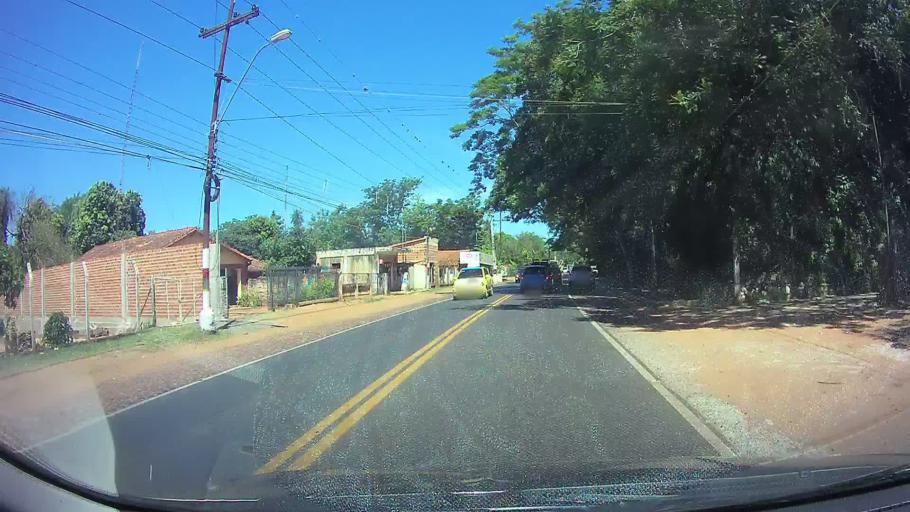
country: PY
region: Central
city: Aregua
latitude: -25.2989
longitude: -57.4111
